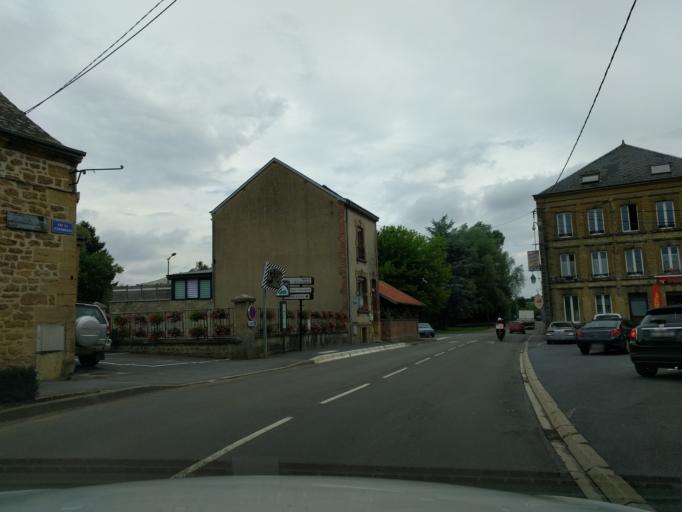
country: FR
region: Champagne-Ardenne
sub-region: Departement des Ardennes
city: Warcq
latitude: 49.7702
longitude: 4.6812
